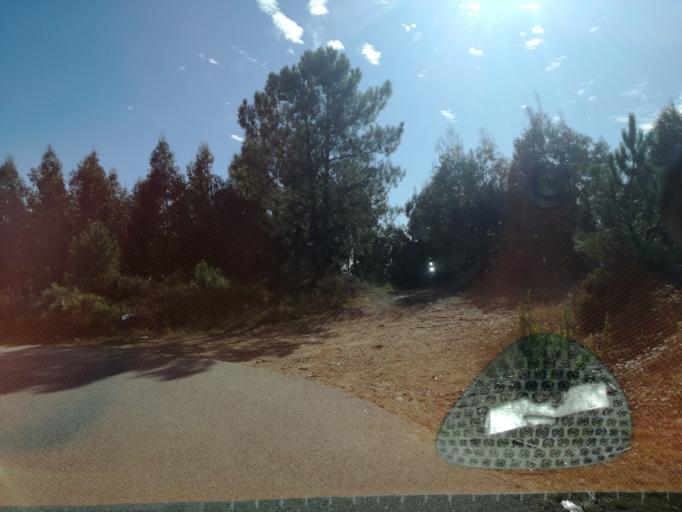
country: PT
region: Porto
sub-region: Pacos de Ferreira
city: Seroa
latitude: 41.2622
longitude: -8.4504
